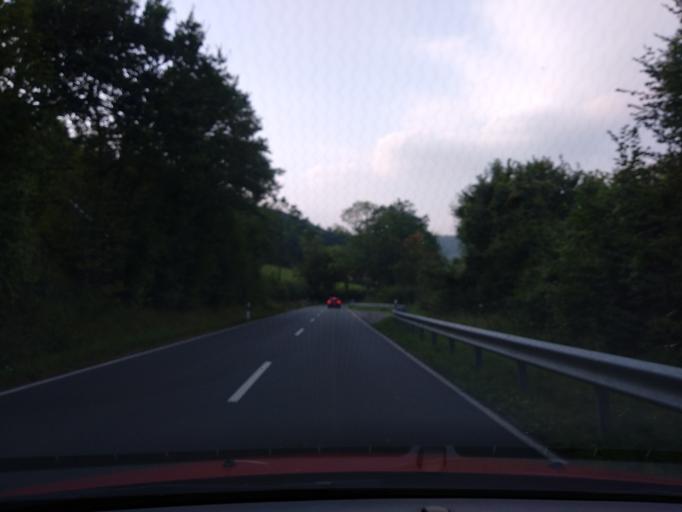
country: DE
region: North Rhine-Westphalia
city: Beverungen
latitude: 51.6444
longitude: 9.3472
